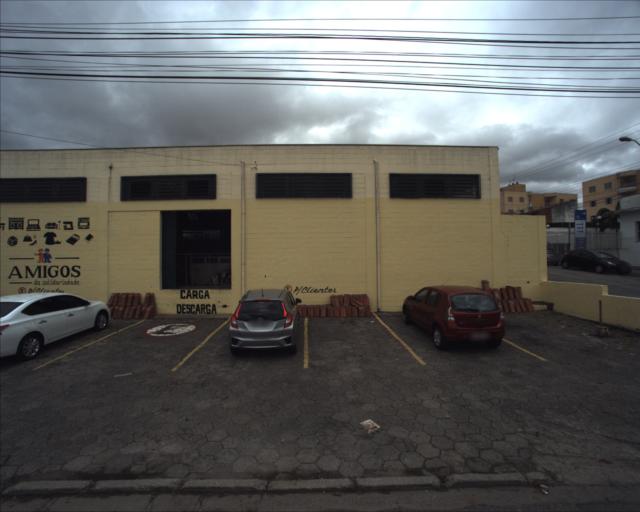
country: BR
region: Sao Paulo
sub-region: Sorocaba
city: Sorocaba
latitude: -23.4794
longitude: -47.4706
